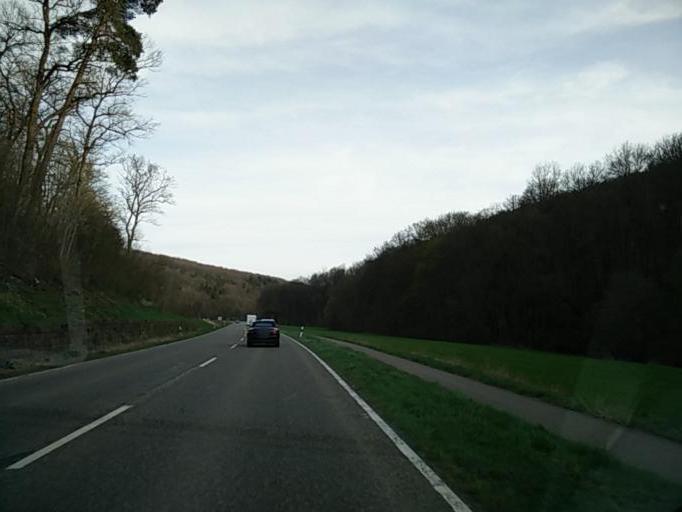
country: DE
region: Baden-Wuerttemberg
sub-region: Tuebingen Region
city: Tuebingen
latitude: 48.5520
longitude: 9.0702
